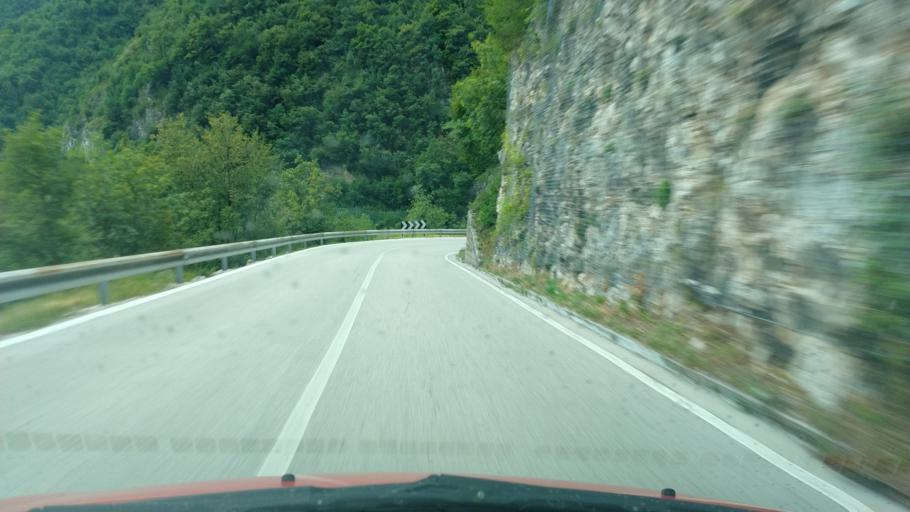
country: IT
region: Veneto
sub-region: Provincia di Vicenza
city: Arsiero
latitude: 45.8165
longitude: 11.3598
